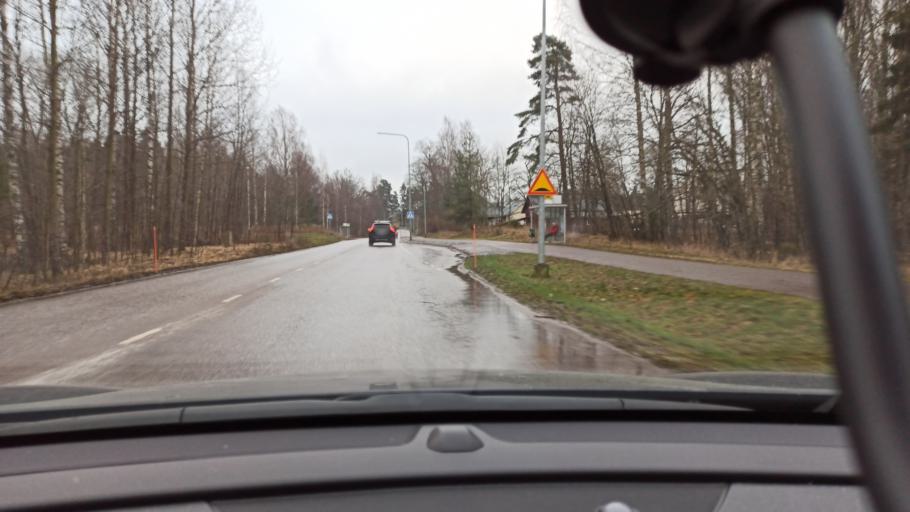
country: FI
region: Uusimaa
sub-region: Helsinki
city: Kirkkonummi
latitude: 60.1333
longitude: 24.4292
